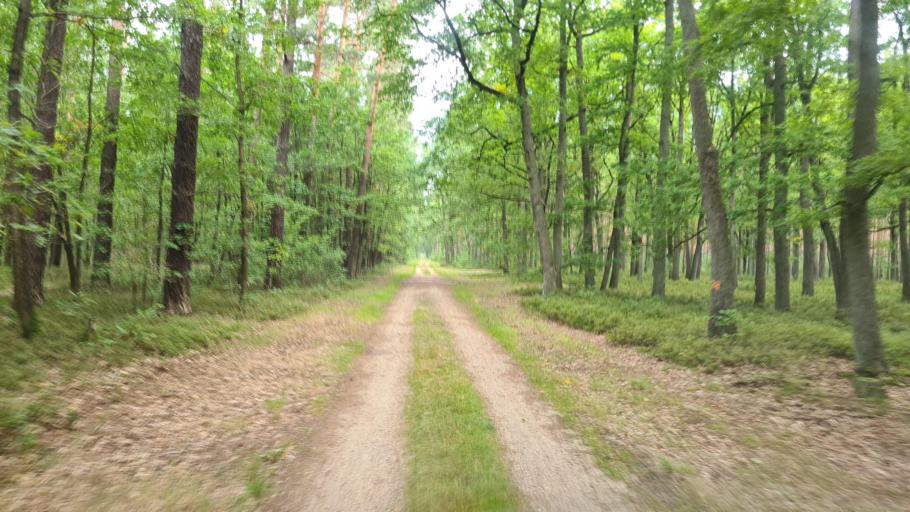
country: DE
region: Brandenburg
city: Hohenbucko
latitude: 51.7855
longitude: 13.5417
